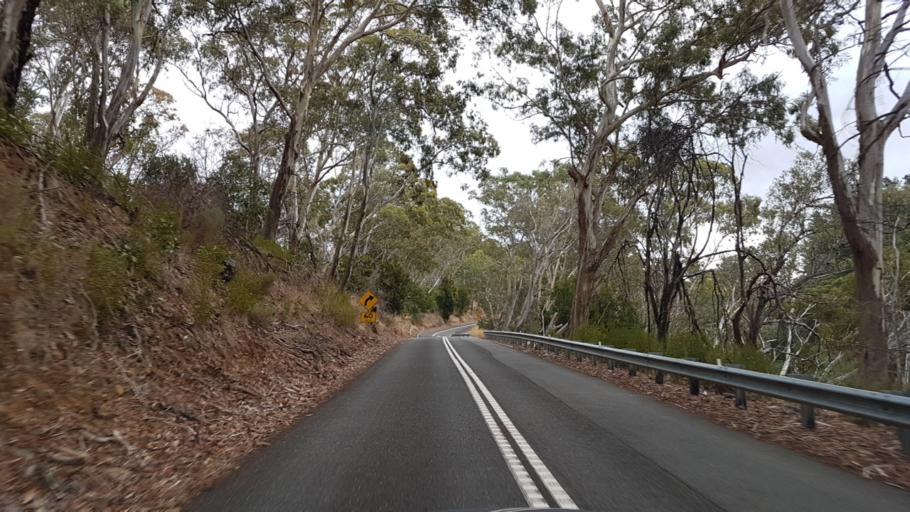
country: AU
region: South Australia
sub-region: Adelaide Hills
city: Gumeracha
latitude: -34.8426
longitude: 138.8385
